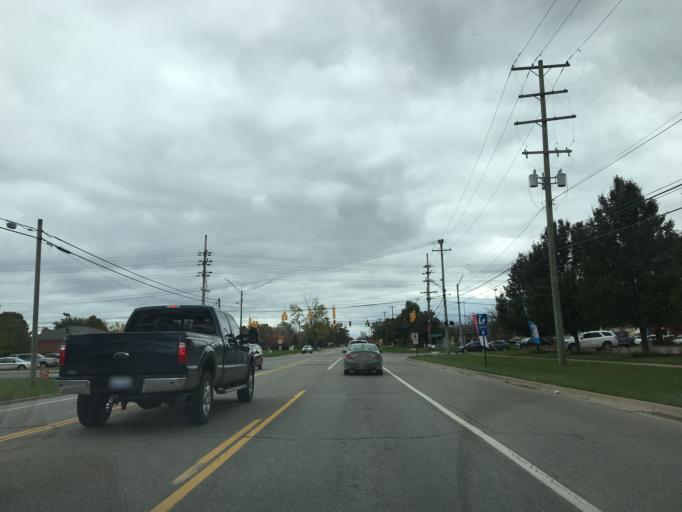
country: US
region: Michigan
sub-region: Oakland County
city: South Lyon
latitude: 42.4474
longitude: -83.6507
